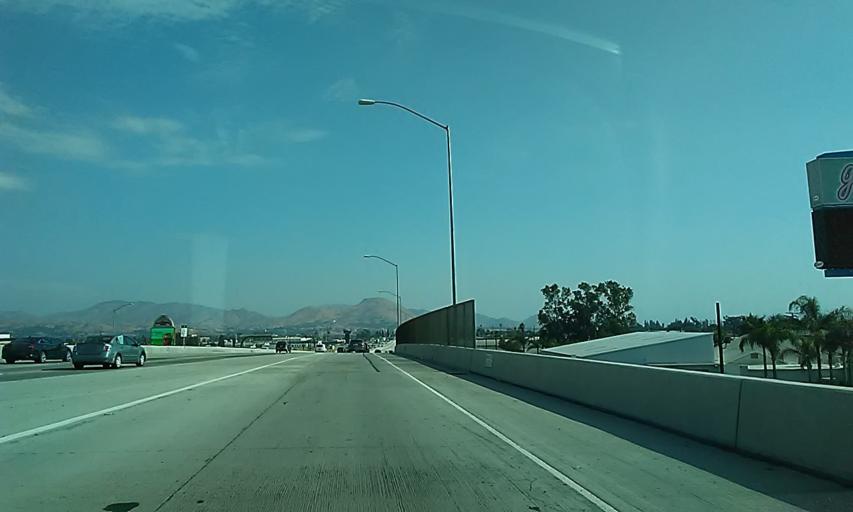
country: US
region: California
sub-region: San Bernardino County
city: San Bernardino
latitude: 34.1006
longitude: -117.3023
